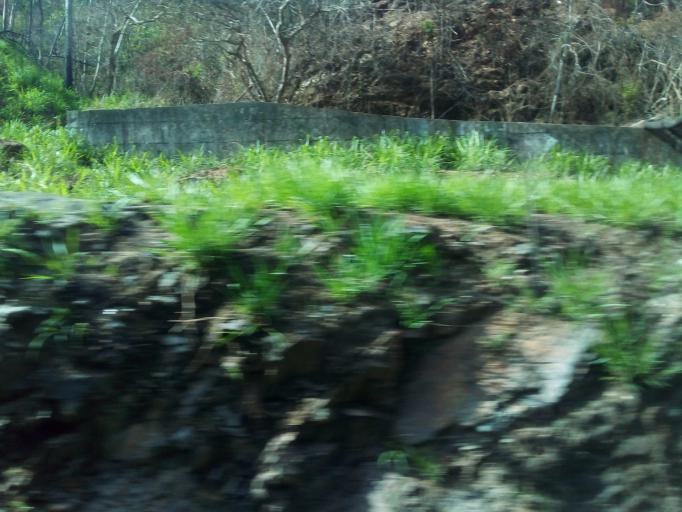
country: BR
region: Minas Gerais
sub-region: Raposos
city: Raposos
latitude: -19.8699
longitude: -43.8277
